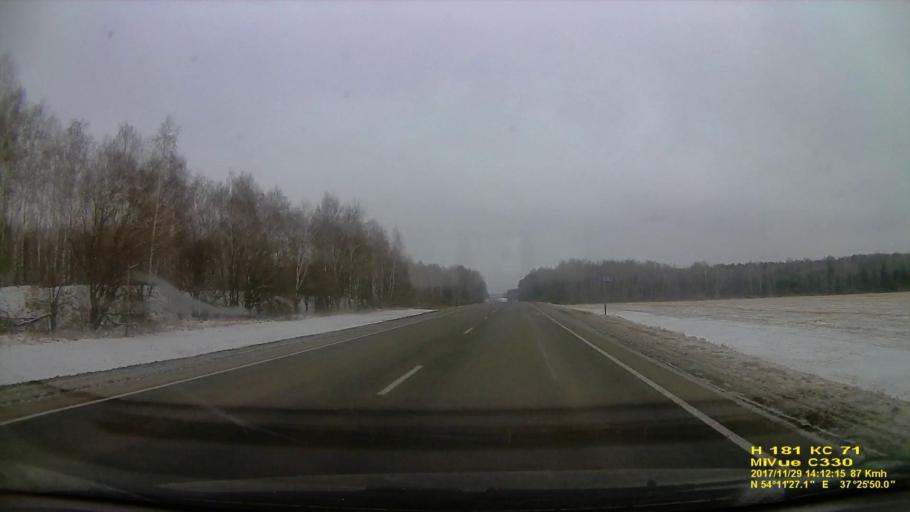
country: RU
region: Tula
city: Barsuki
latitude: 54.1907
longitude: 37.4309
